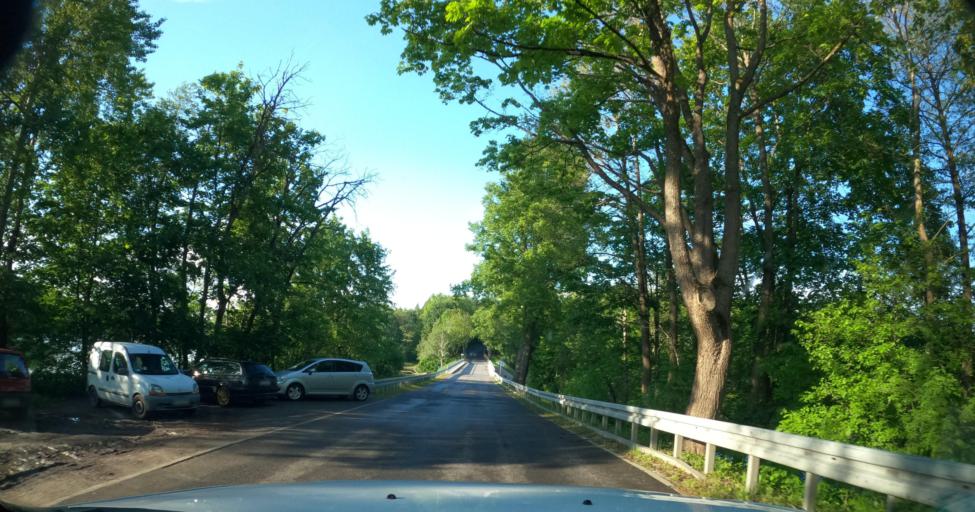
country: PL
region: Warmian-Masurian Voivodeship
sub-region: Powiat braniewski
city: Braniewo
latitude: 54.2801
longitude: 19.8484
